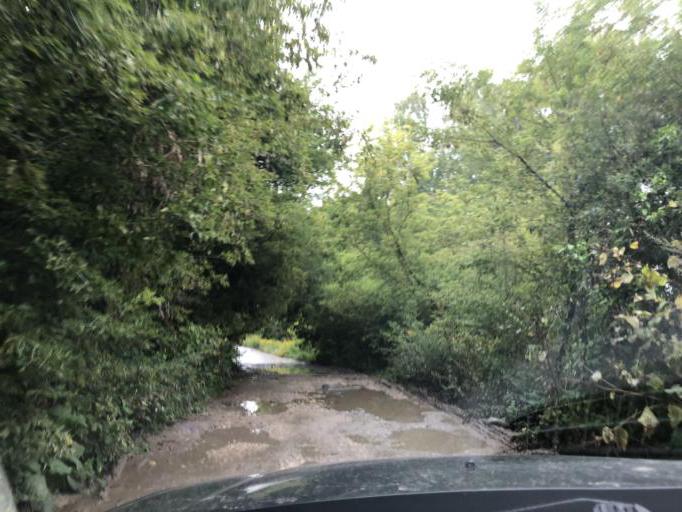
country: RU
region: Tula
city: Mendeleyevskiy
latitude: 54.1692
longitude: 37.5514
